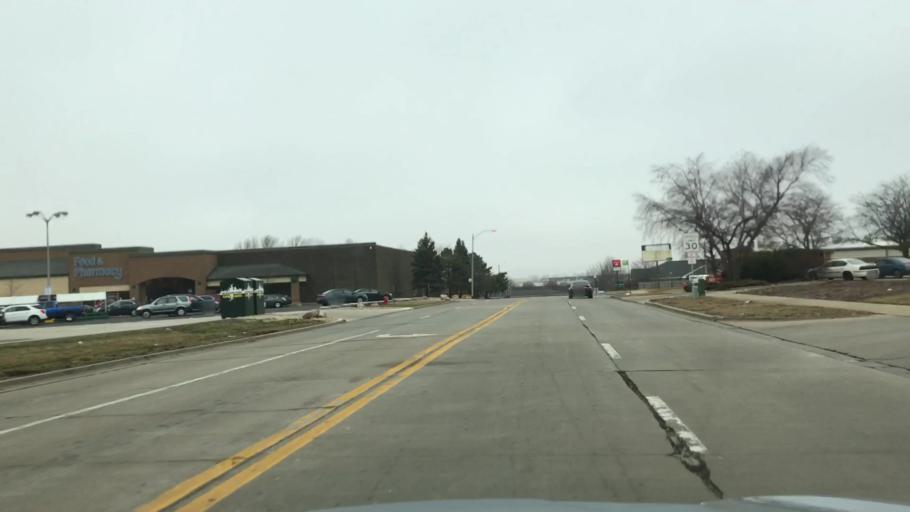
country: US
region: Illinois
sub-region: McLean County
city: Normal
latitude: 40.5106
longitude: -88.9554
